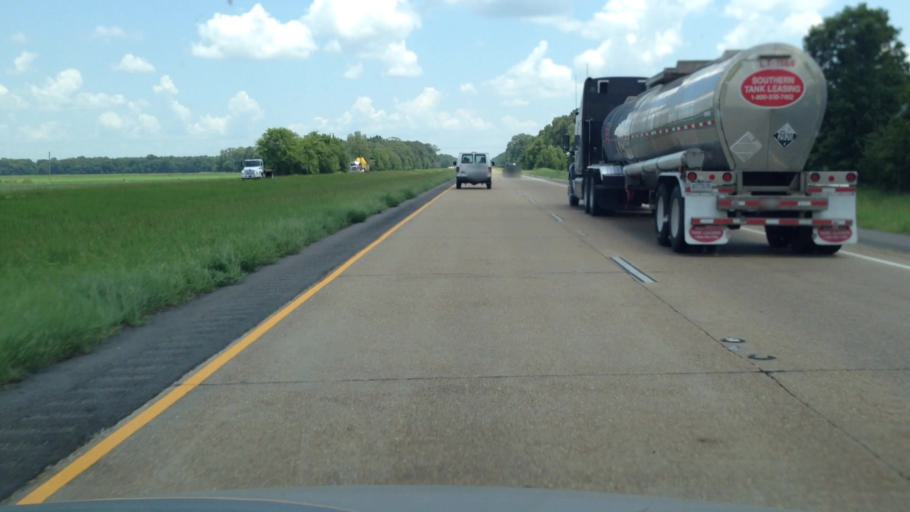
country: US
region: Louisiana
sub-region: Rapides Parish
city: Lecompte
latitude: 31.0033
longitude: -92.3478
